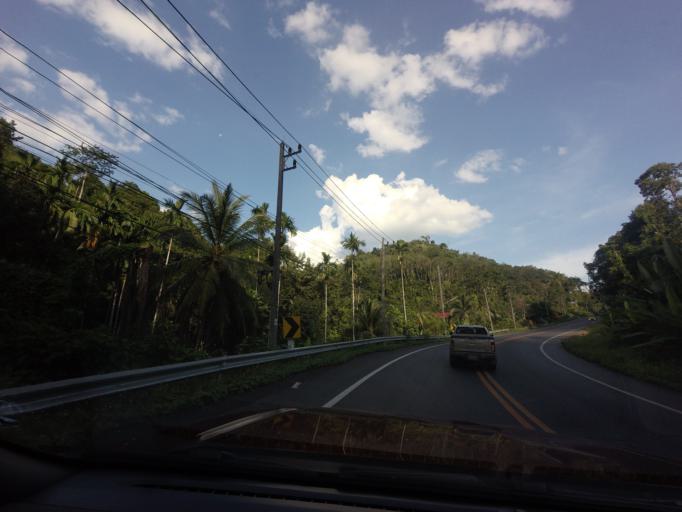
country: TH
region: Yala
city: Than To
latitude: 6.2095
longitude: 101.1684
